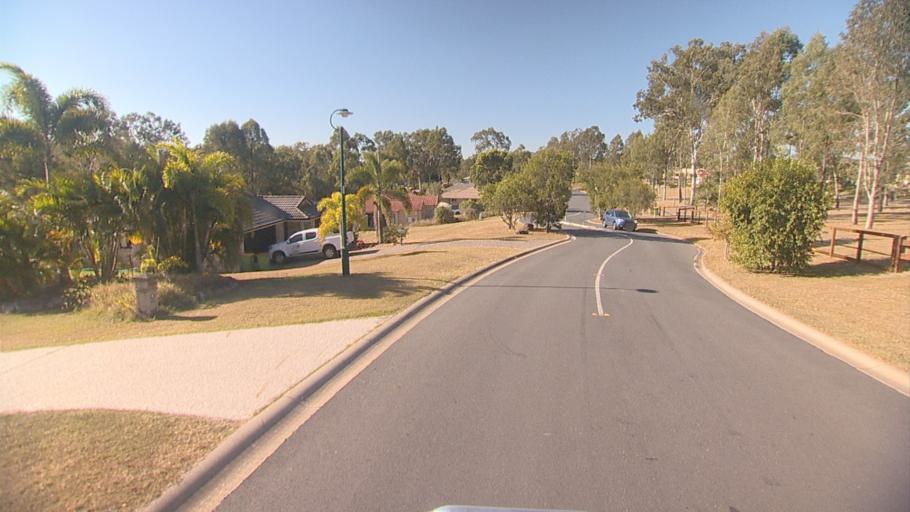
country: AU
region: Queensland
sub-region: Logan
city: Cedar Vale
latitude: -27.8646
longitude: 153.0361
